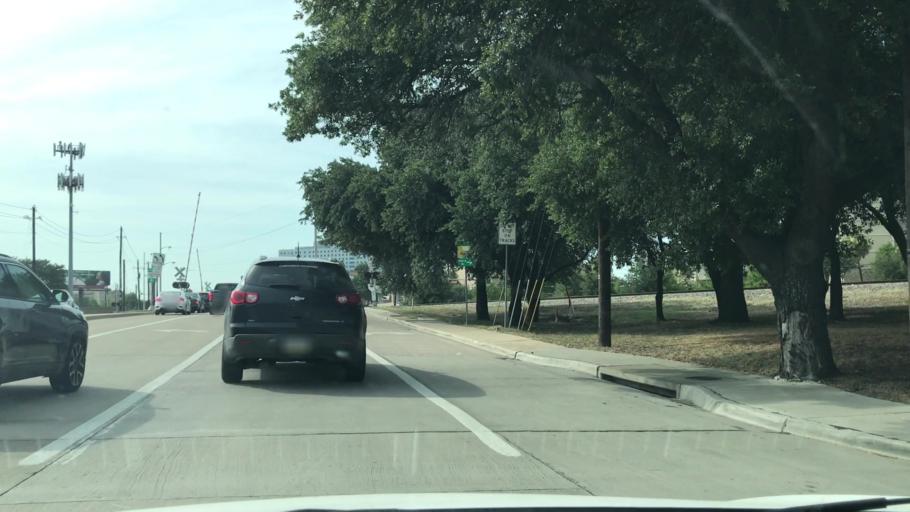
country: US
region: Texas
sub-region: Dallas County
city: Dallas
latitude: 32.8049
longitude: -96.8290
